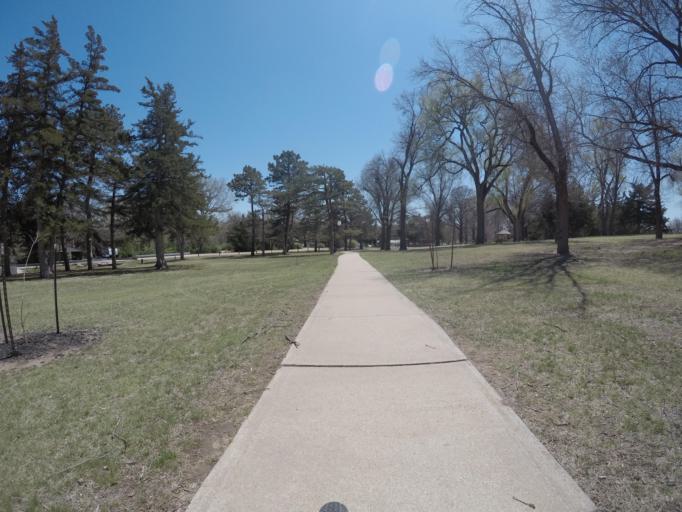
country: US
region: Kansas
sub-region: Pratt County
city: Pratt
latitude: 37.6398
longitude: -98.7310
